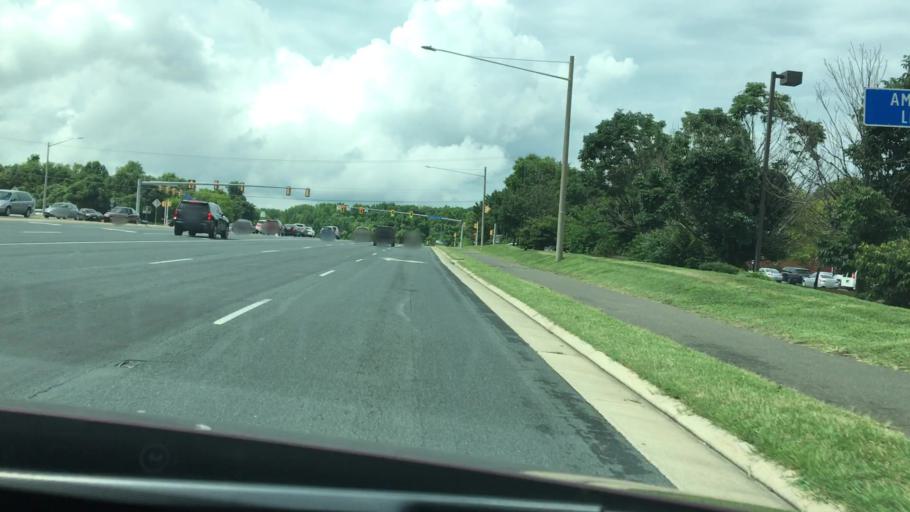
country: US
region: Virginia
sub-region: Prince William County
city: Dale City
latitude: 38.6515
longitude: -77.3161
